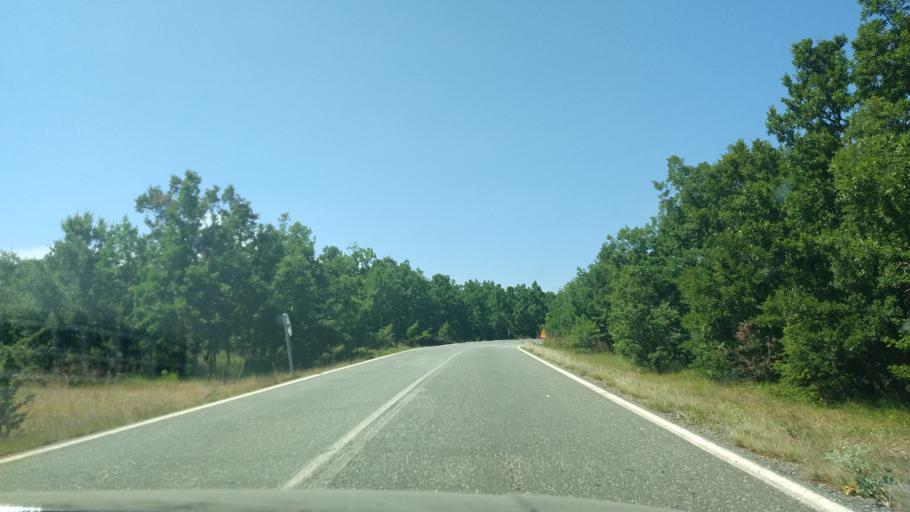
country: GR
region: West Macedonia
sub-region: Nomos Grevenon
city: Grevena
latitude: 40.0145
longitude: 21.4871
